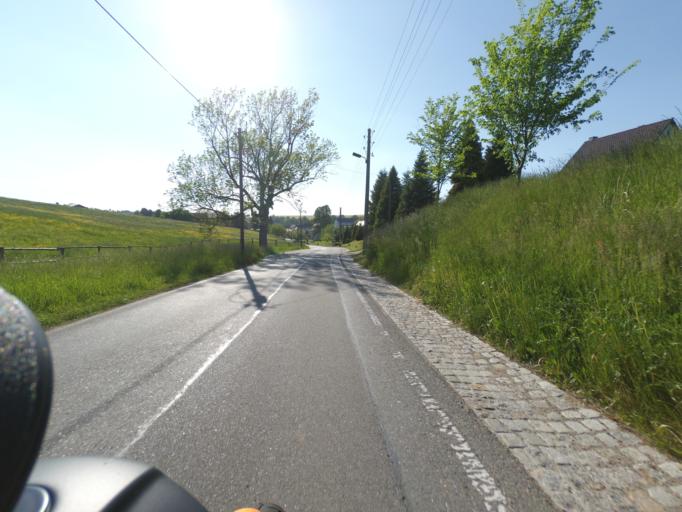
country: DE
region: Saxony
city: Rabenau
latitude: 50.9724
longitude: 13.6710
